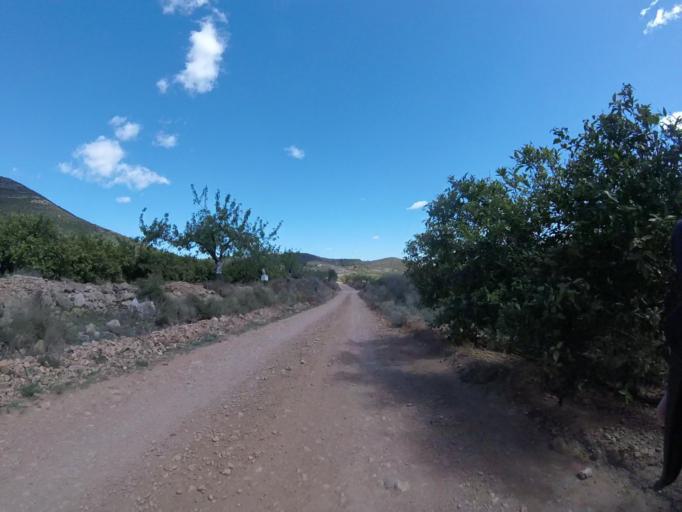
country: ES
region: Valencia
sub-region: Provincia de Castello
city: Orpesa/Oropesa del Mar
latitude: 40.1670
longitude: 0.1400
